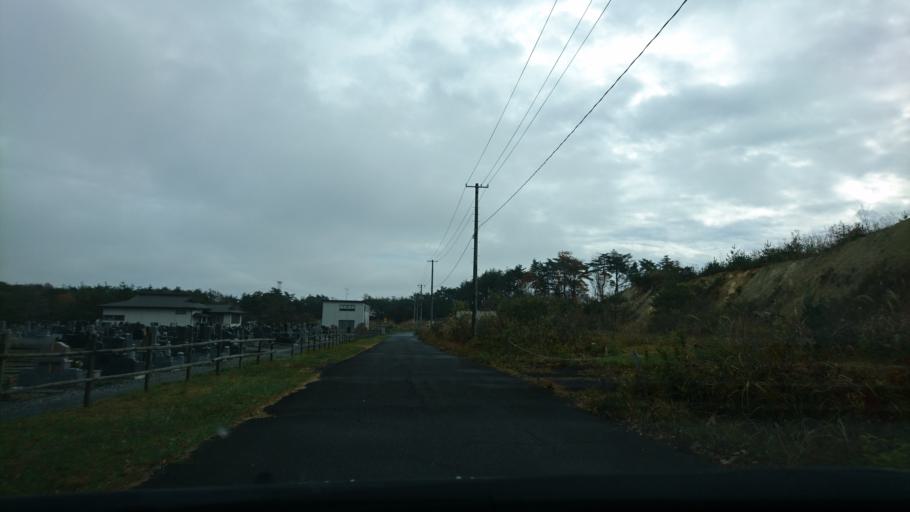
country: JP
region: Iwate
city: Ichinoseki
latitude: 38.8780
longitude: 141.1509
